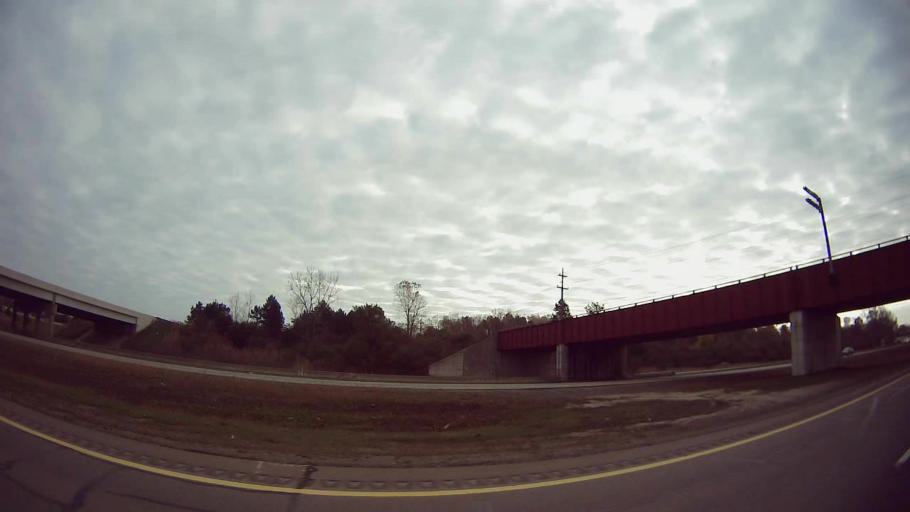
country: US
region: Michigan
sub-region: Wayne County
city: Romulus
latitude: 42.2198
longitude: -83.4121
